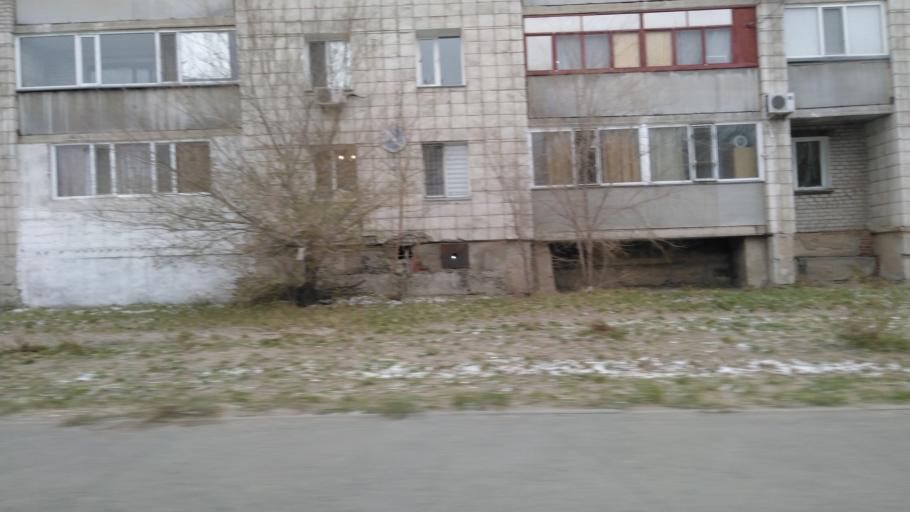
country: KZ
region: Pavlodar
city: Pavlodar
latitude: 52.2768
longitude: 76.9621
